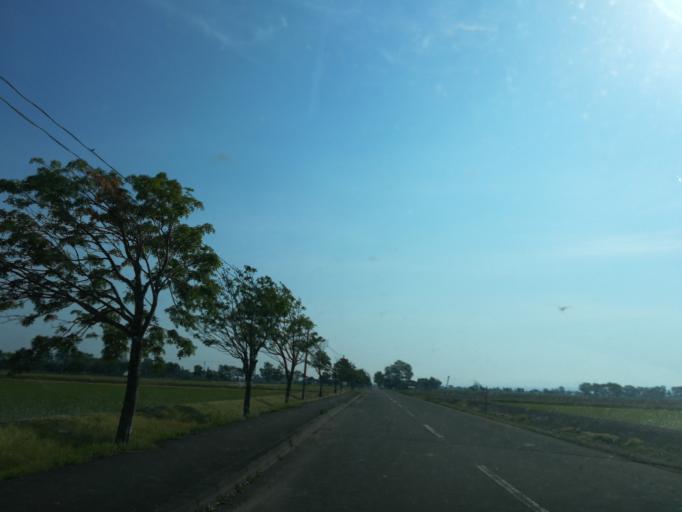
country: JP
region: Hokkaido
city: Iwamizawa
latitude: 43.1518
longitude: 141.6687
